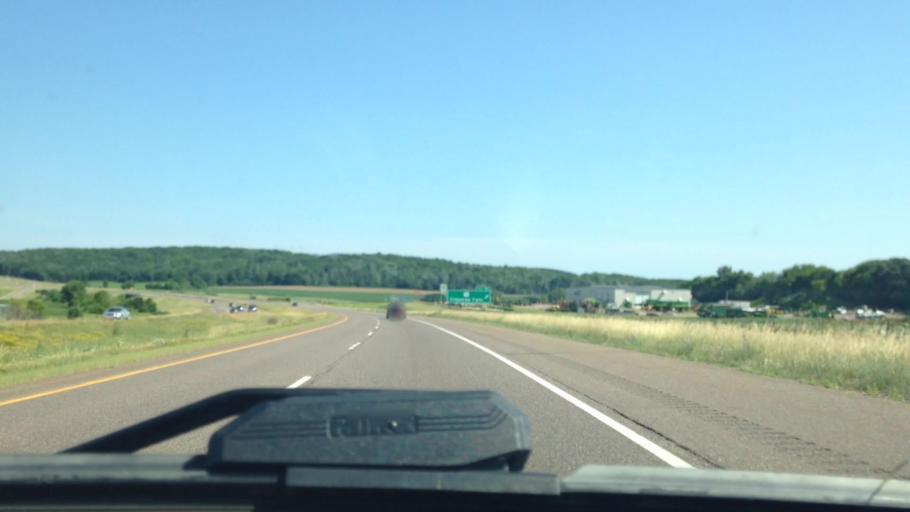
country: US
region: Wisconsin
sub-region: Chippewa County
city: Chippewa Falls
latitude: 44.9588
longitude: -91.4252
